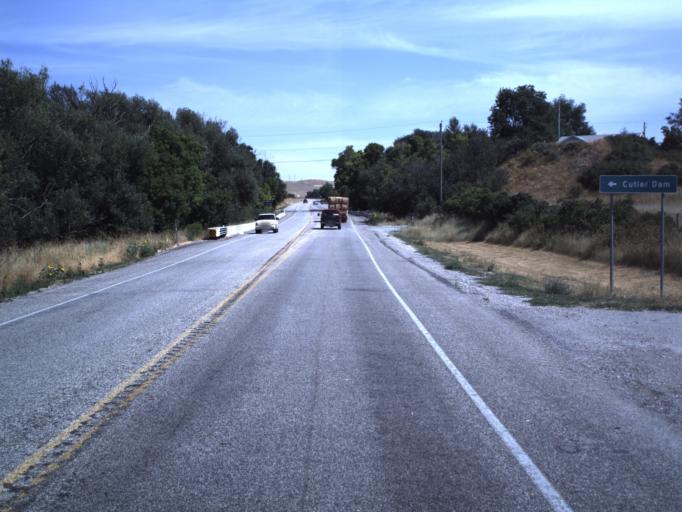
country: US
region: Utah
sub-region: Cache County
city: Mendon
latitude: 41.7960
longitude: -112.0428
